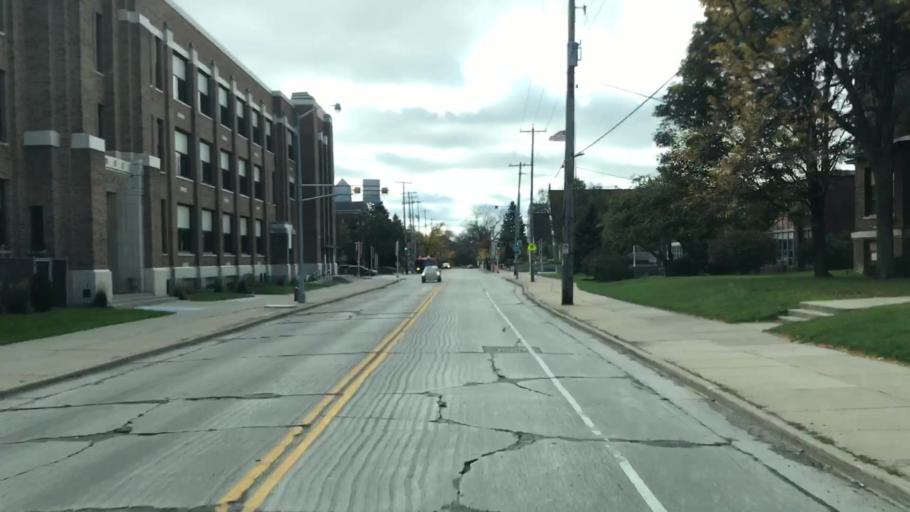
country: US
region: Wisconsin
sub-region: Milwaukee County
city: Wauwatosa
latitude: 43.0538
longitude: -88.0074
